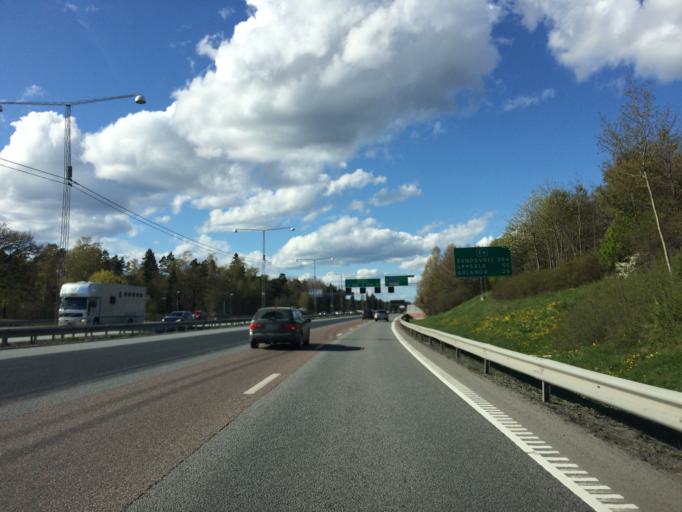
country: SE
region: Stockholm
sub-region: Sollentuna Kommun
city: Sollentuna
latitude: 59.4226
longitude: 17.9249
